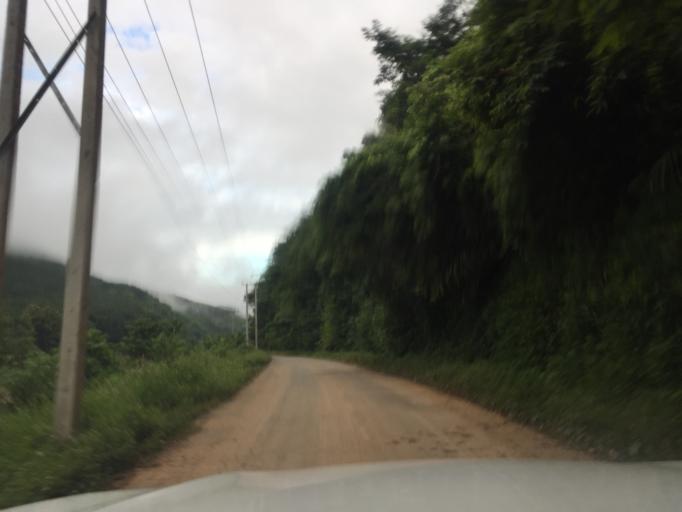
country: LA
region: Phongsali
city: Khoa
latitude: 21.0781
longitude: 102.3769
